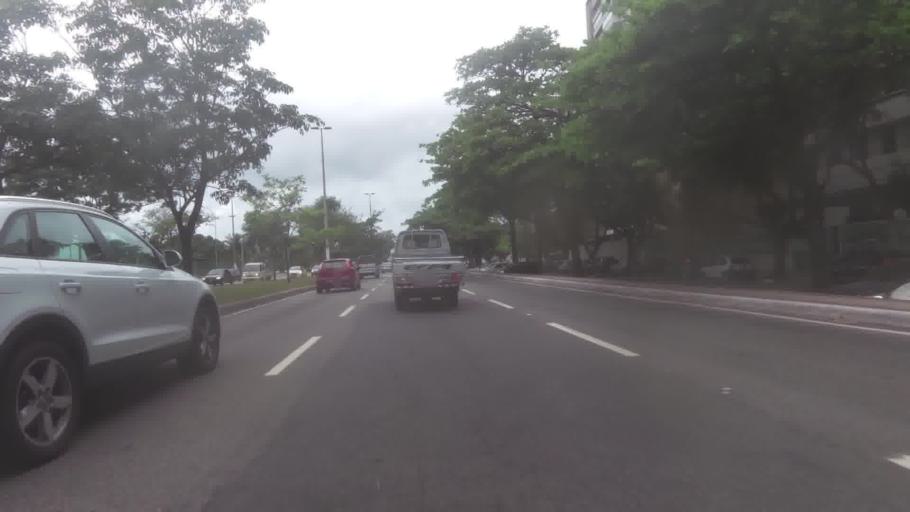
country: BR
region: Espirito Santo
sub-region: Vila Velha
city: Vila Velha
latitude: -20.3005
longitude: -40.2922
